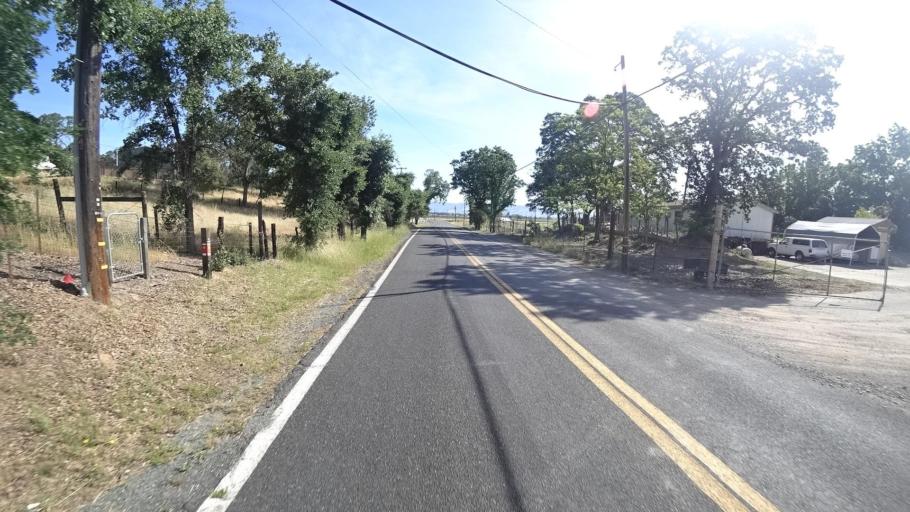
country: US
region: California
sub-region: Lake County
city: Kelseyville
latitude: 38.9708
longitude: -122.8964
